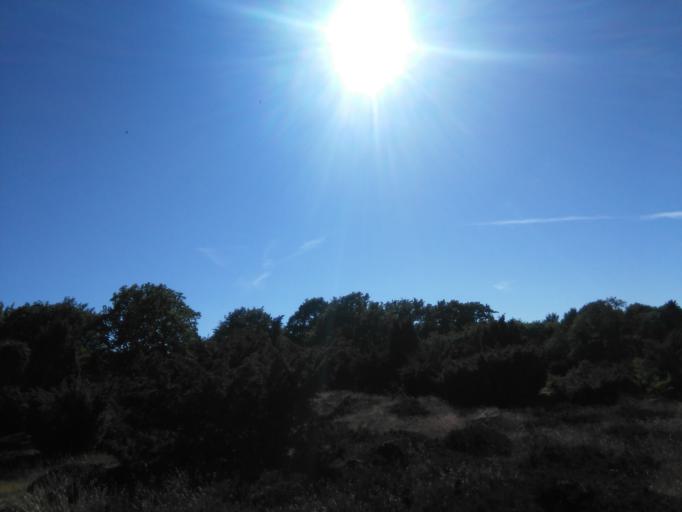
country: DK
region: Capital Region
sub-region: Bornholm Kommune
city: Ronne
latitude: 55.2610
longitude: 14.7675
